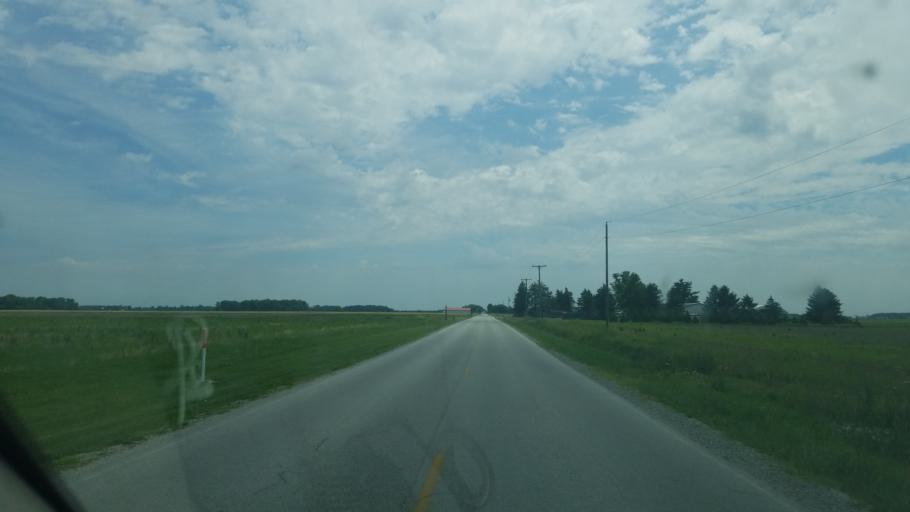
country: US
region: Ohio
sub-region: Wood County
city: Bowling Green
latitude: 41.2967
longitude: -83.6233
